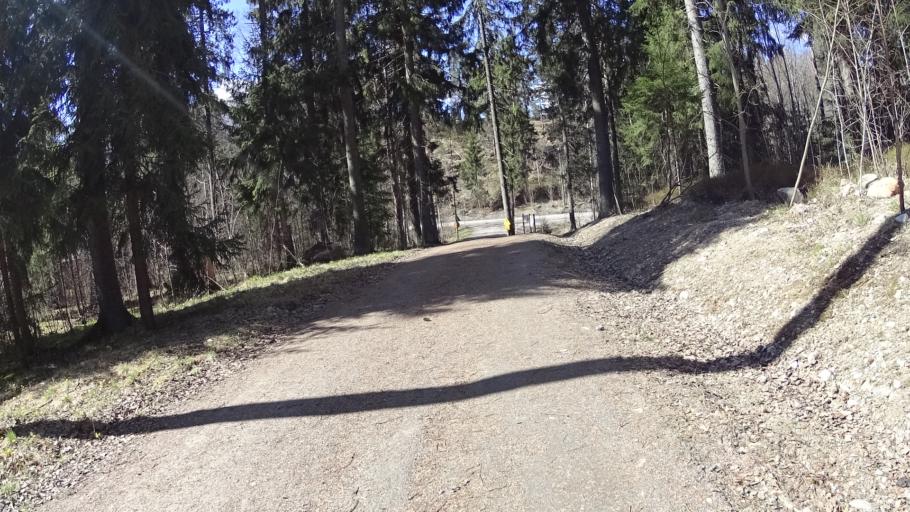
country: FI
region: Uusimaa
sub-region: Helsinki
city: Espoo
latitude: 60.2295
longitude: 24.6234
